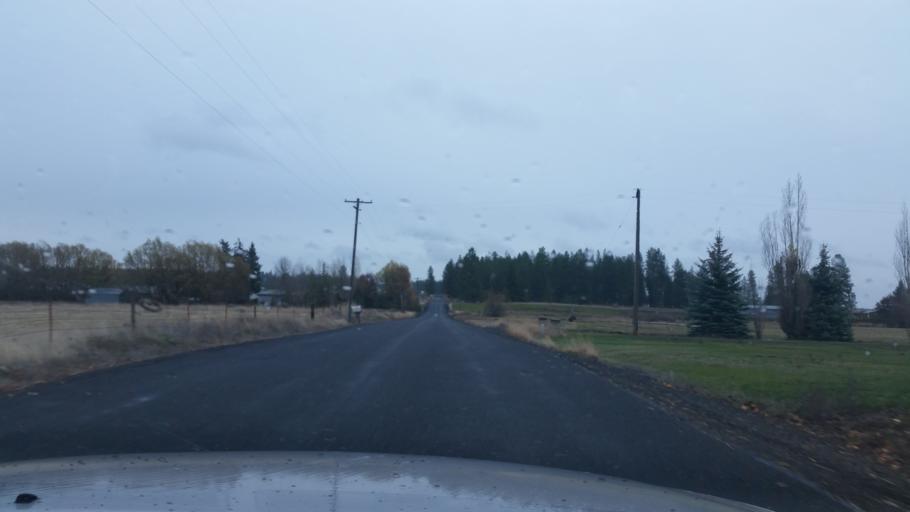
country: US
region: Washington
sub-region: Spokane County
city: Medical Lake
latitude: 47.6143
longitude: -117.7414
